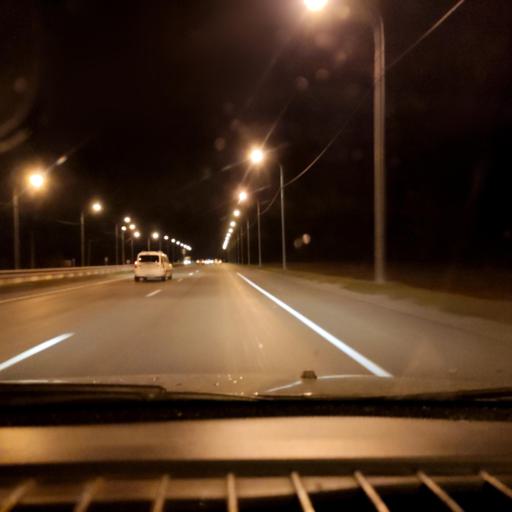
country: RU
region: Samara
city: Tol'yatti
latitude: 53.5746
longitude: 49.4462
